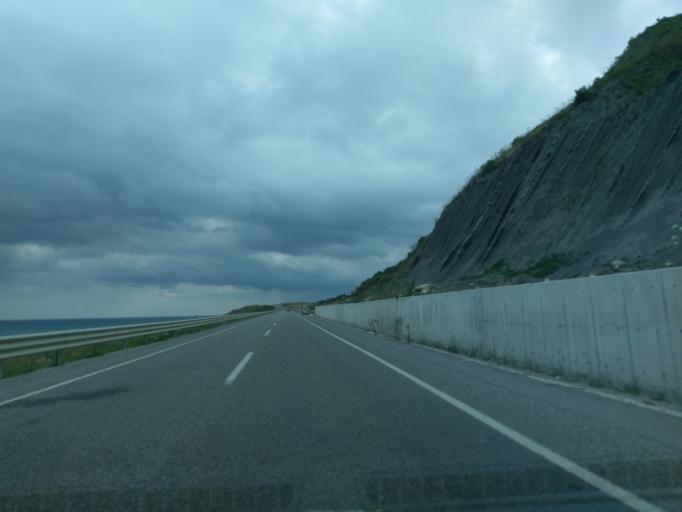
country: TR
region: Sinop
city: Helaldi
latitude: 41.9488
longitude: 34.3712
